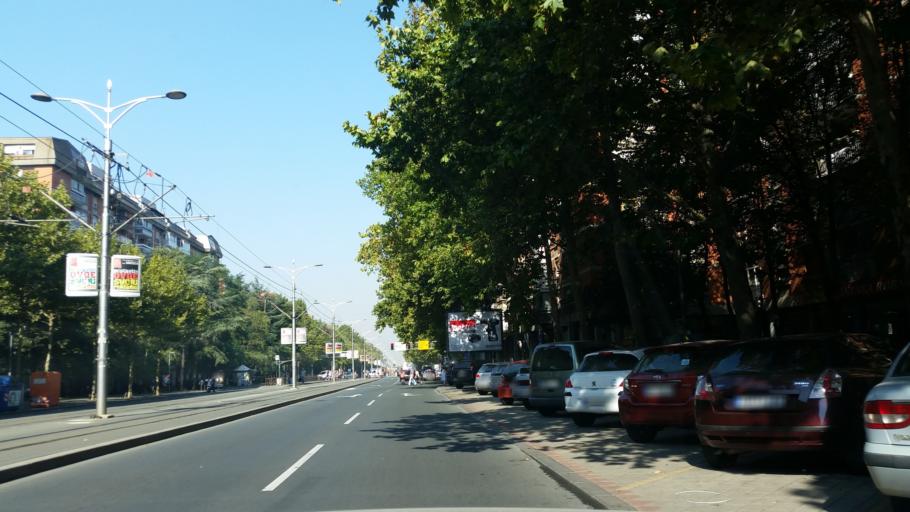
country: RS
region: Central Serbia
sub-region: Belgrade
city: Palilula
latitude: 44.7949
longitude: 20.5008
